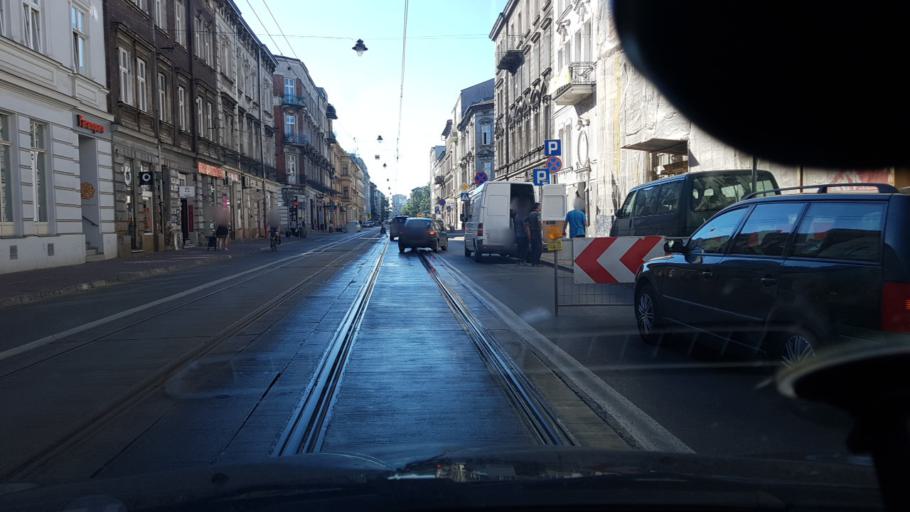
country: PL
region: Lesser Poland Voivodeship
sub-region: Krakow
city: Krakow
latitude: 50.0553
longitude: 19.9466
